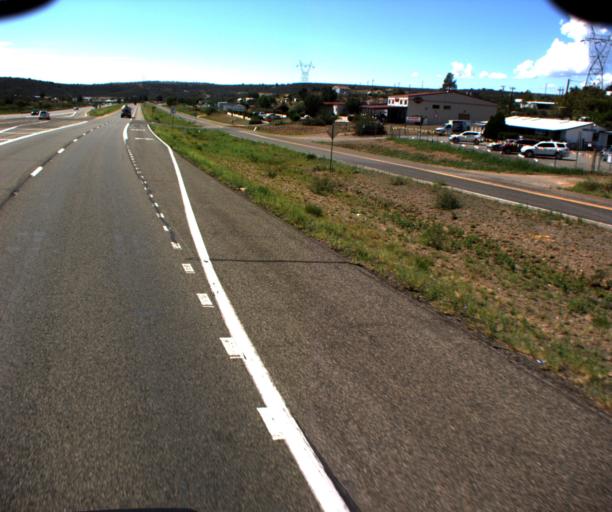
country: US
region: Arizona
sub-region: Yavapai County
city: Mayer
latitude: 34.3949
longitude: -112.2232
